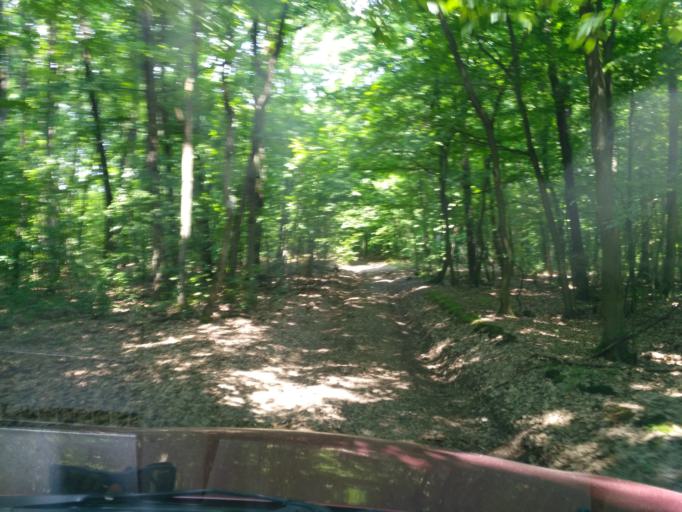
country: SK
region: Kosicky
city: Moldava nad Bodvou
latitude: 48.6343
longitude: 21.0429
